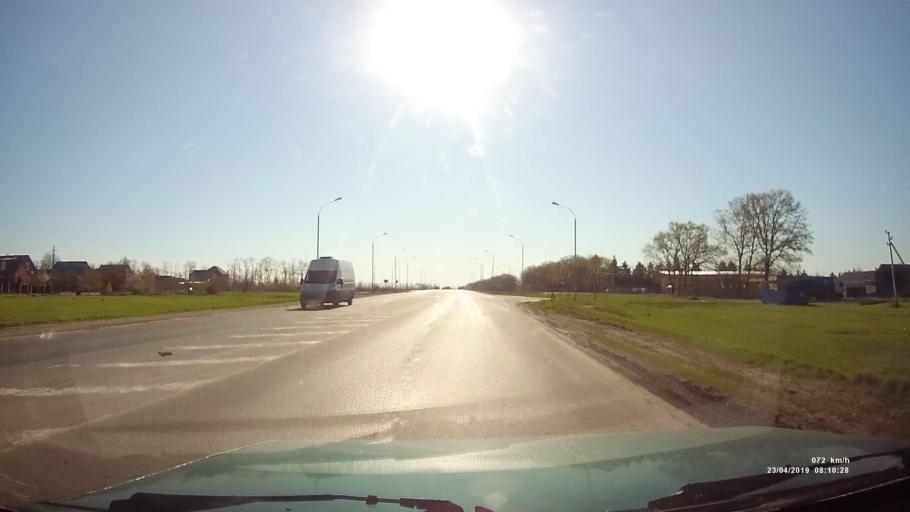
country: RU
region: Rostov
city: Yegorlykskaya
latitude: 46.5551
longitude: 40.6818
